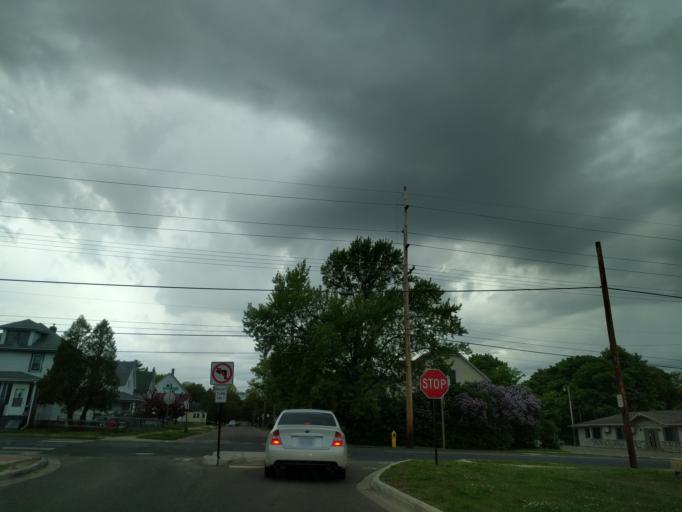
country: US
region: Michigan
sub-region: Marquette County
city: Marquette
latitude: 46.5591
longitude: -87.3959
